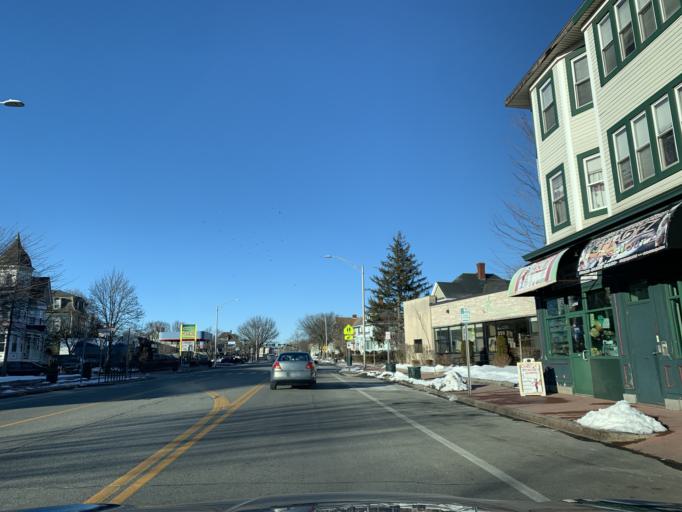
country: US
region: Rhode Island
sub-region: Providence County
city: Providence
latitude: 41.8049
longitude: -71.4253
